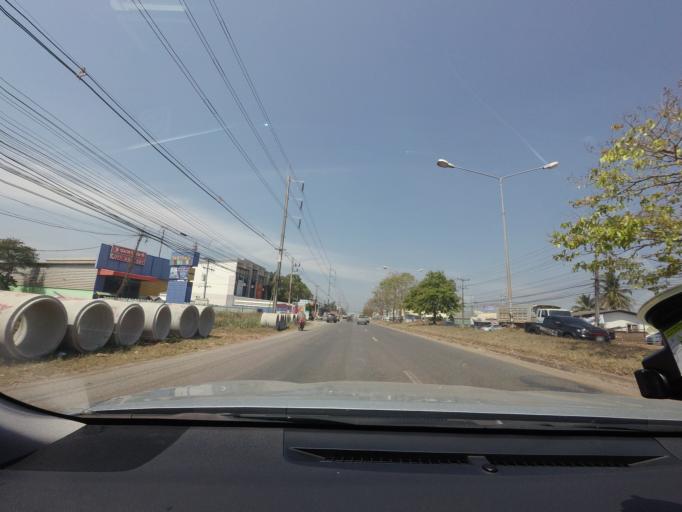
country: TH
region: Surat Thani
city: Surat Thani
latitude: 9.1480
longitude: 99.3954
